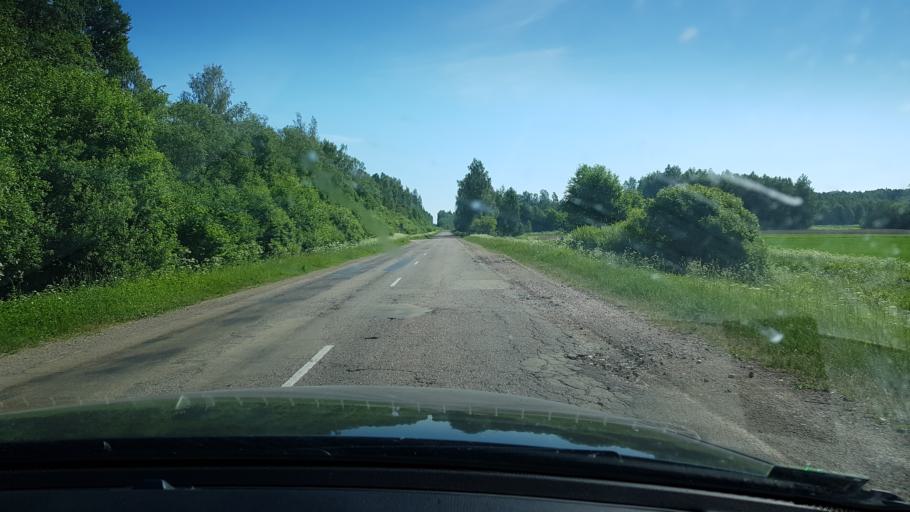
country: LV
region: Daugavpils
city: Daugavpils
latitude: 55.8178
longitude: 26.7408
